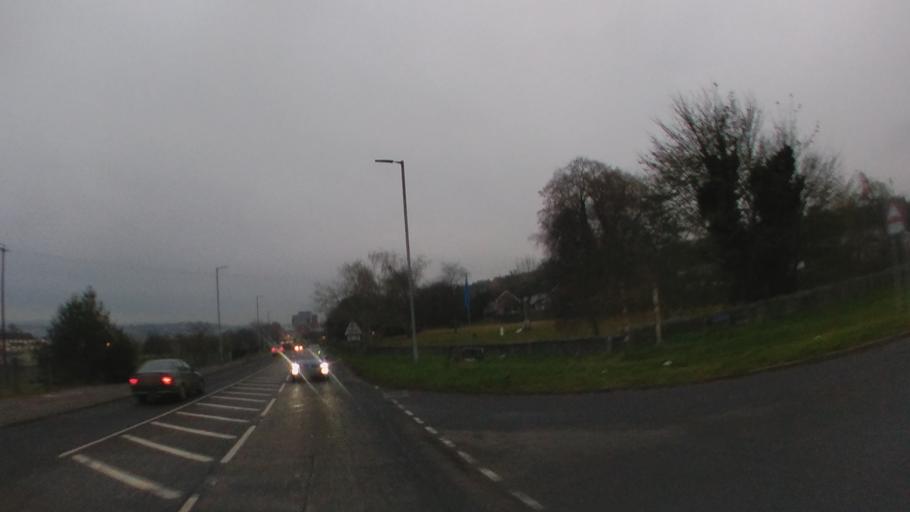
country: GB
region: Northern Ireland
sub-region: Newry and Mourne District
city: Newry
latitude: 54.1837
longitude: -6.3556
